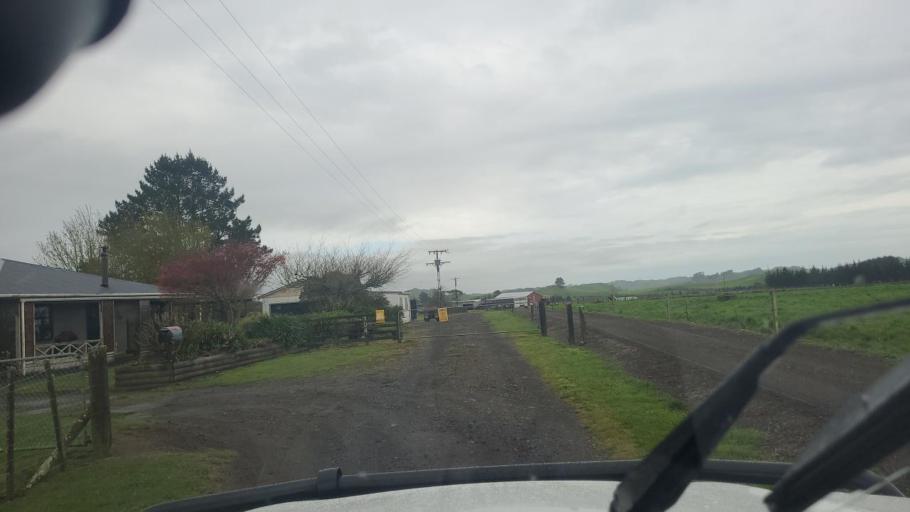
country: NZ
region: Taranaki
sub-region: South Taranaki District
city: Eltham
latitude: -39.3506
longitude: 174.3837
